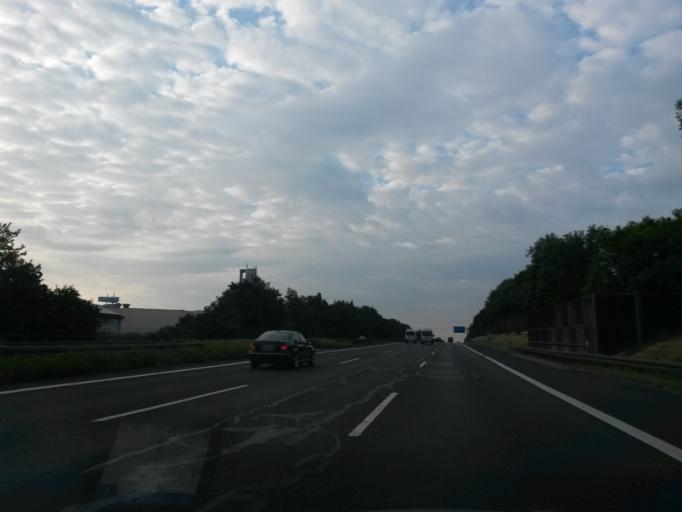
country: DE
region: Bavaria
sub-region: Upper Bavaria
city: Denkendorf
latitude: 48.9339
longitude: 11.4579
